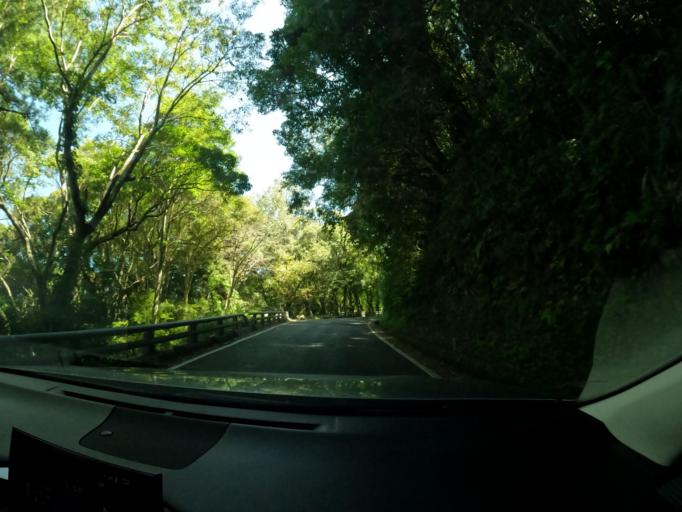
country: TW
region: Taiwan
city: Yujing
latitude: 23.2847
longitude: 120.9020
